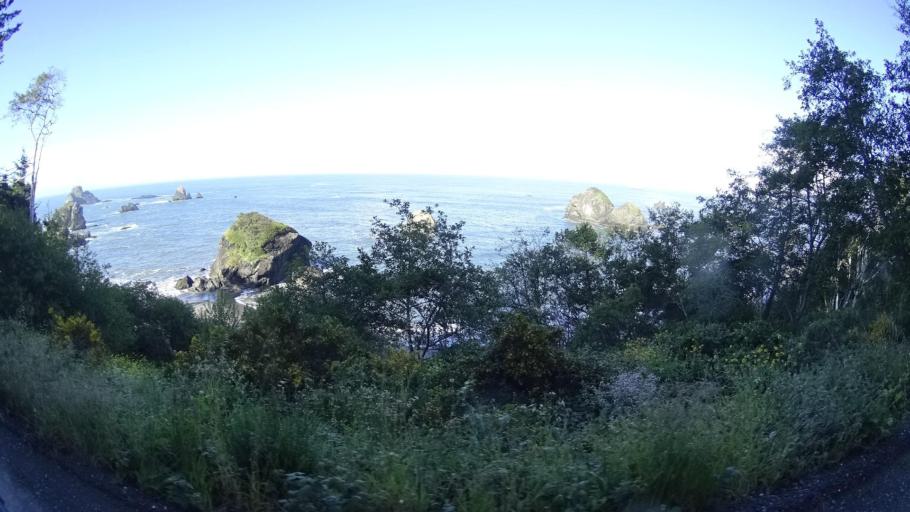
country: US
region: California
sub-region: Humboldt County
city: Westhaven-Moonstone
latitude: 41.0434
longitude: -124.1205
